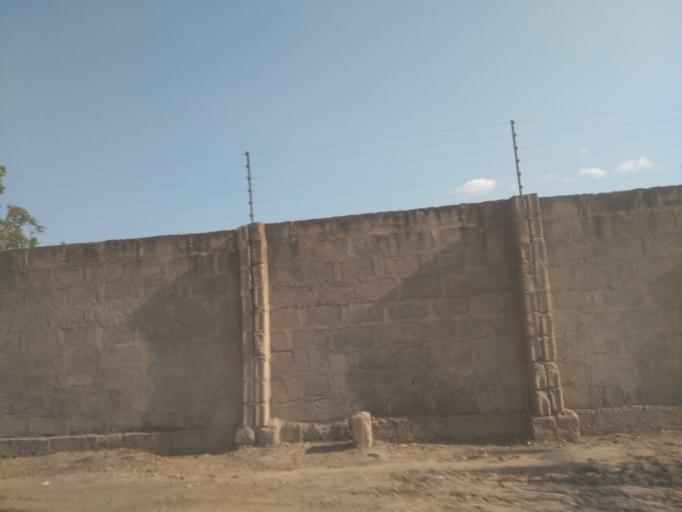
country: TZ
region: Dar es Salaam
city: Dar es Salaam
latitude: -6.8487
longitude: 39.3192
